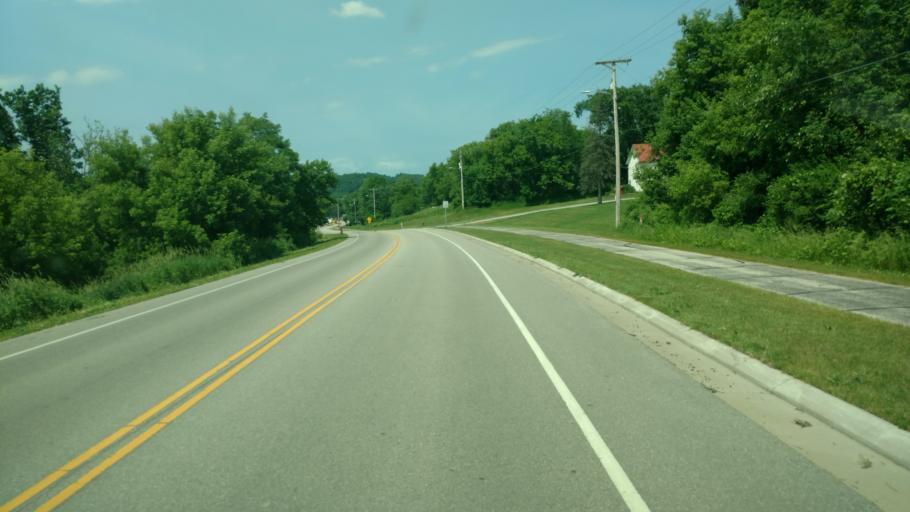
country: US
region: Wisconsin
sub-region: Vernon County
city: Viroqua
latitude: 43.4985
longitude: -90.6799
